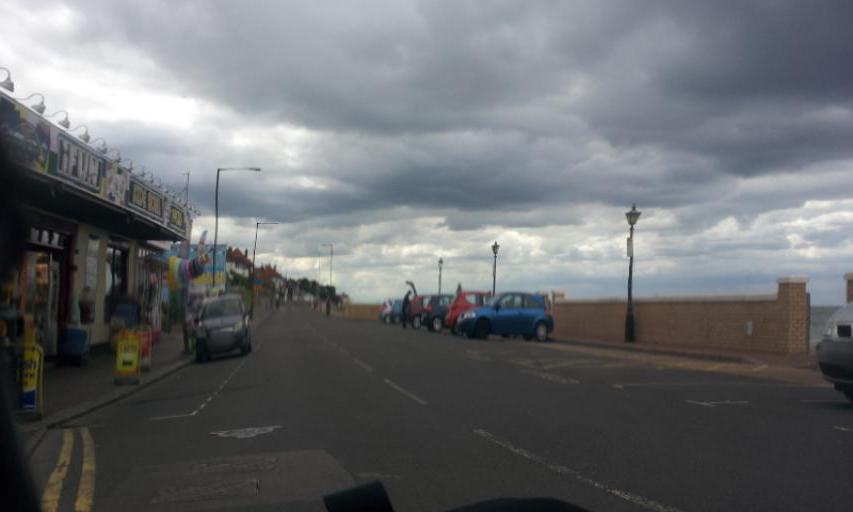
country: GB
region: England
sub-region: Kent
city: Herne Bay
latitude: 51.3718
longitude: 1.1180
